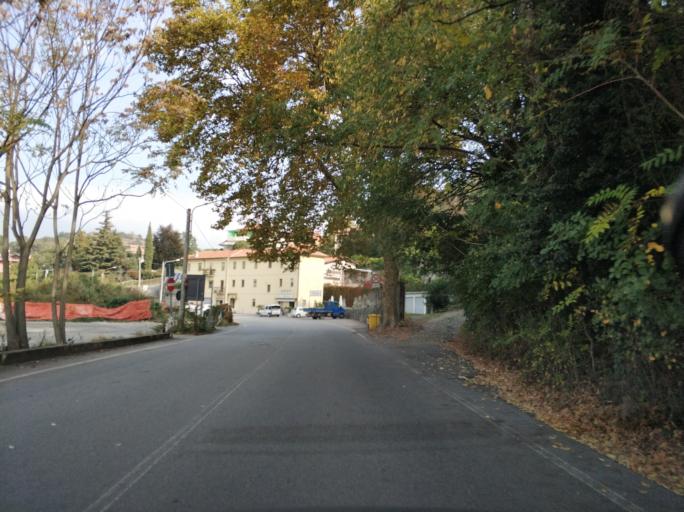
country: IT
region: Piedmont
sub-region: Provincia di Torino
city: Ivrea
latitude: 45.4727
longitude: 7.8806
